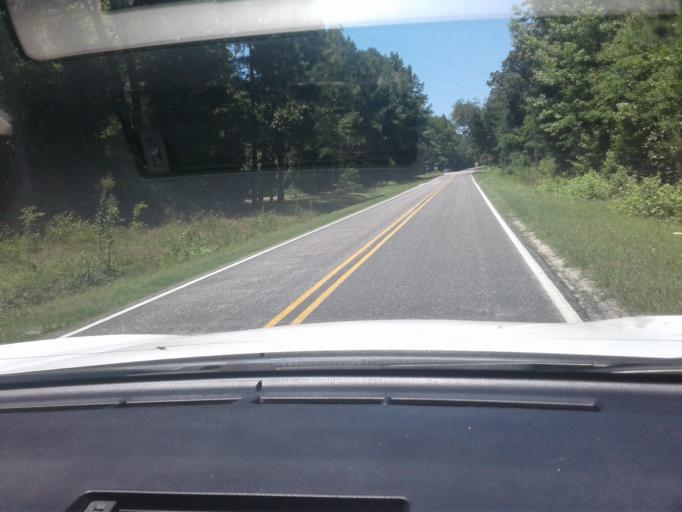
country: US
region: North Carolina
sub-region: Harnett County
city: Lillington
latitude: 35.3519
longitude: -78.9120
